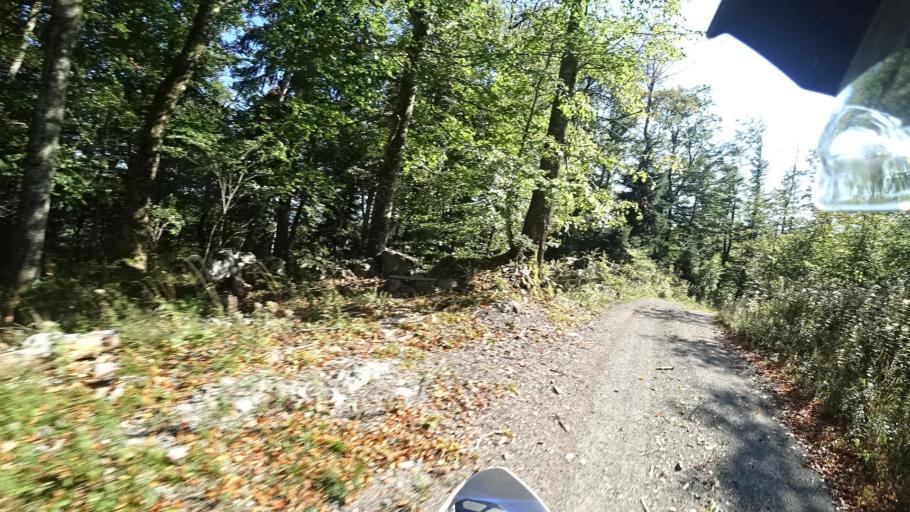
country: HR
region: Primorsko-Goranska
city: Vrbovsko
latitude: 45.2874
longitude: 15.1266
